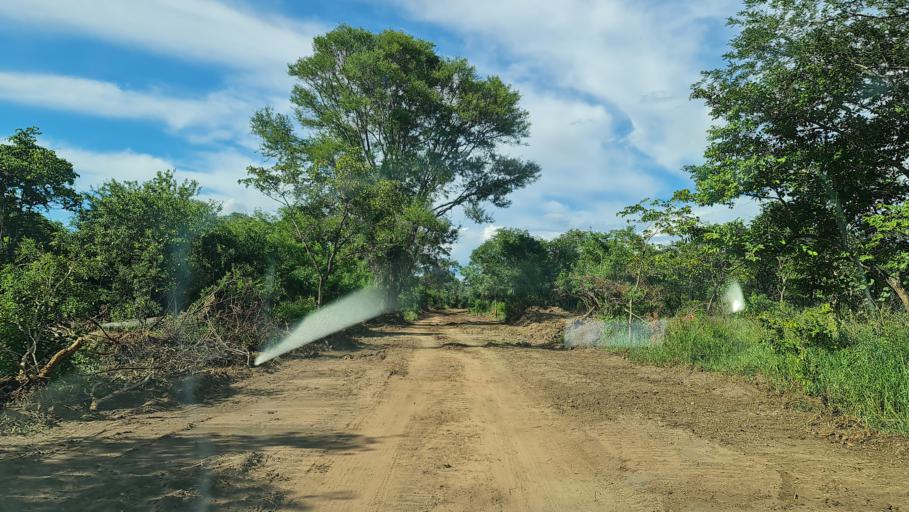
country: MZ
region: Nampula
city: Antonio Enes
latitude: -15.5239
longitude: 40.1273
